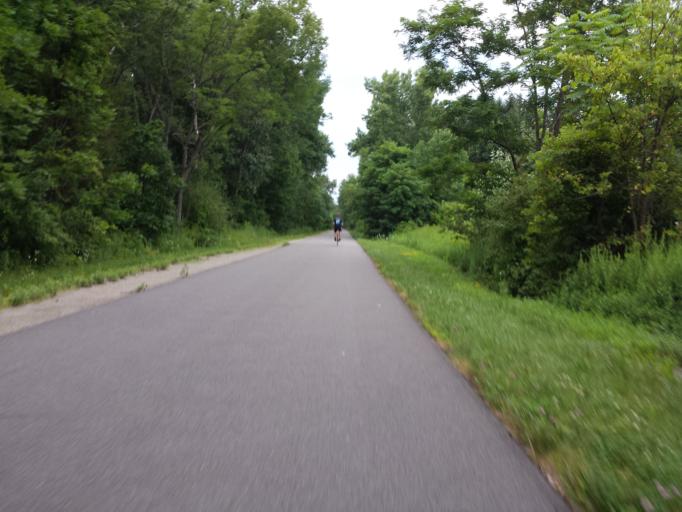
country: US
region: New York
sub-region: Dutchess County
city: Red Oaks Mill
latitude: 41.6735
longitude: -73.8589
